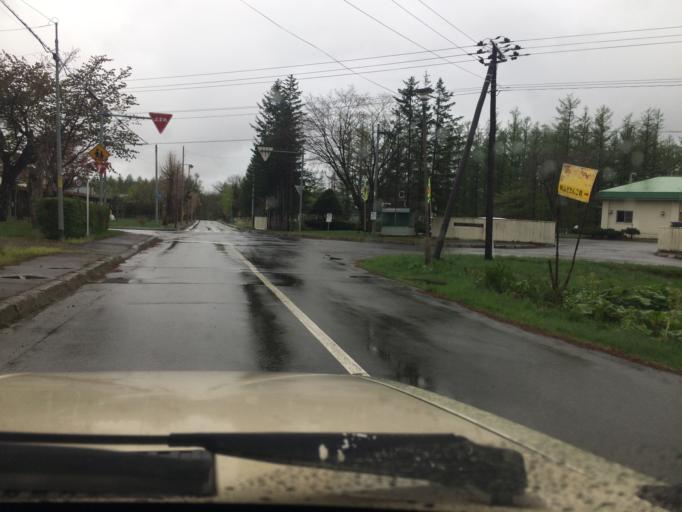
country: JP
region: Hokkaido
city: Obihiro
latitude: 42.8044
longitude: 142.9543
